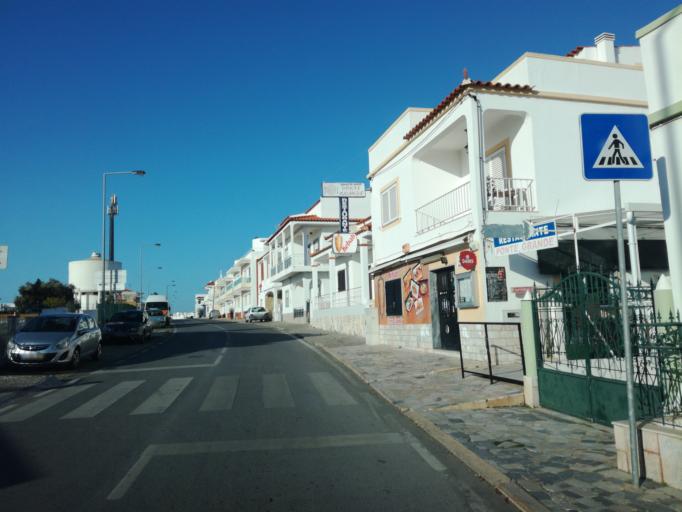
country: PT
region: Faro
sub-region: Olhao
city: Laranjeiro
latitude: 37.0551
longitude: -7.7497
